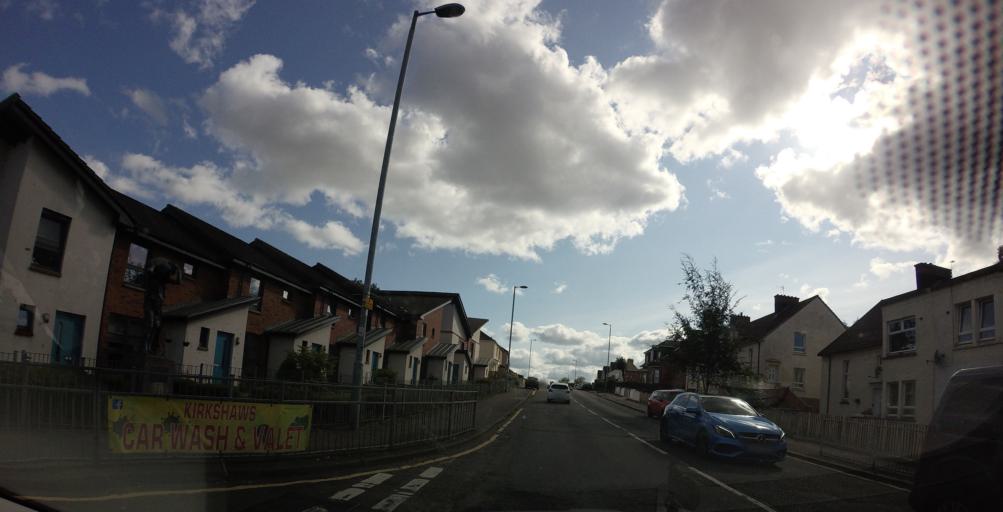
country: GB
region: Scotland
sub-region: North Lanarkshire
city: Coatbridge
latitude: 55.8511
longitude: -4.0477
